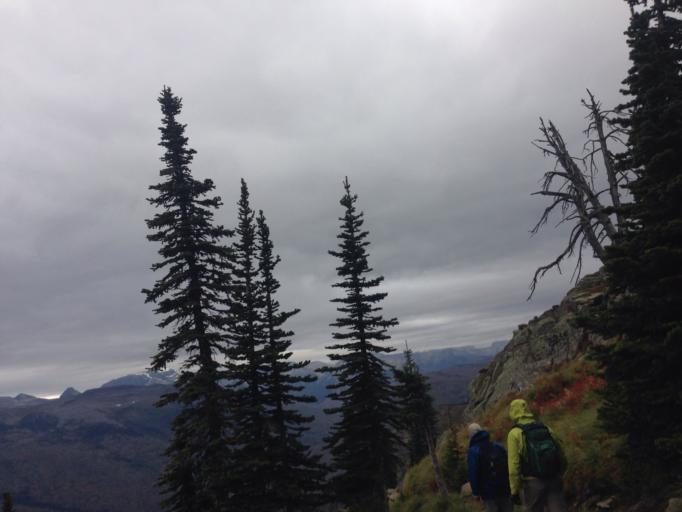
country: US
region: Montana
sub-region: Flathead County
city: Columbia Falls
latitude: 48.7458
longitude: -113.7450
